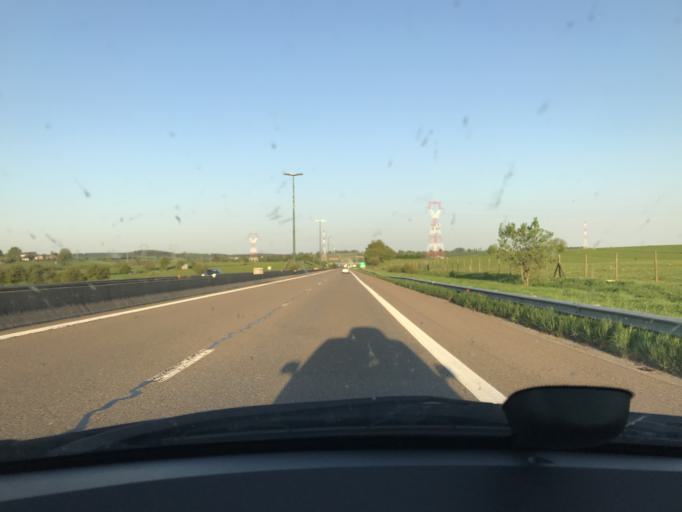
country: BE
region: Wallonia
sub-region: Province du Luxembourg
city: Neufchateau
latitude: 49.8780
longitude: 5.4608
